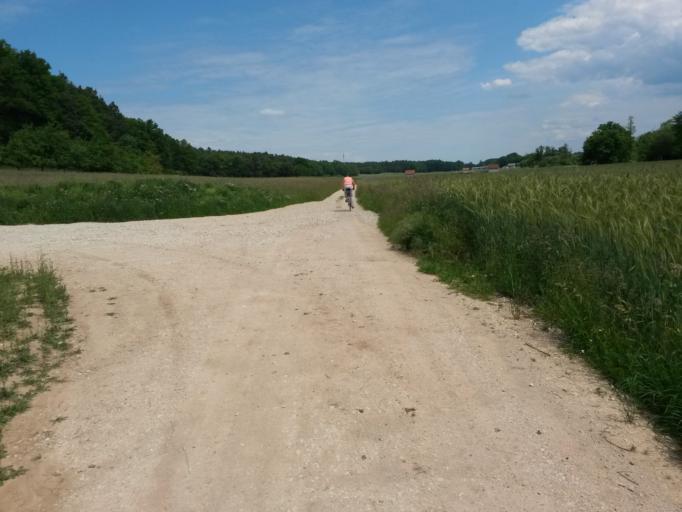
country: DE
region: Bavaria
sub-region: Regierungsbezirk Mittelfranken
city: Rosstal
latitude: 49.4285
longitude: 10.8978
